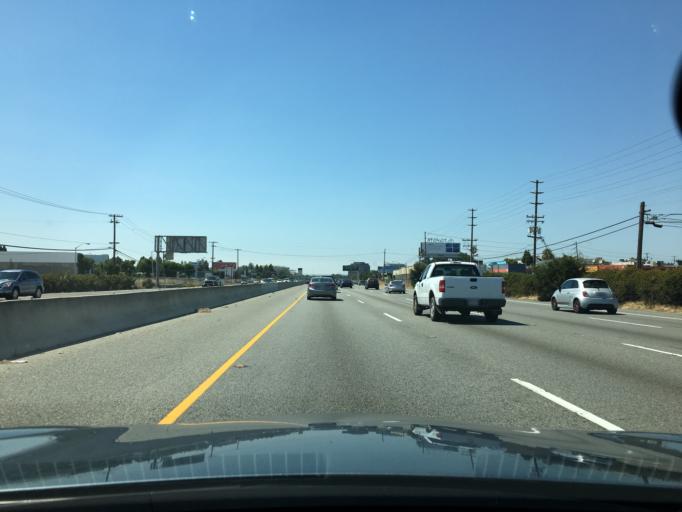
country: US
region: California
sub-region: Santa Clara County
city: Santa Clara
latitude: 37.3796
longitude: -121.9554
